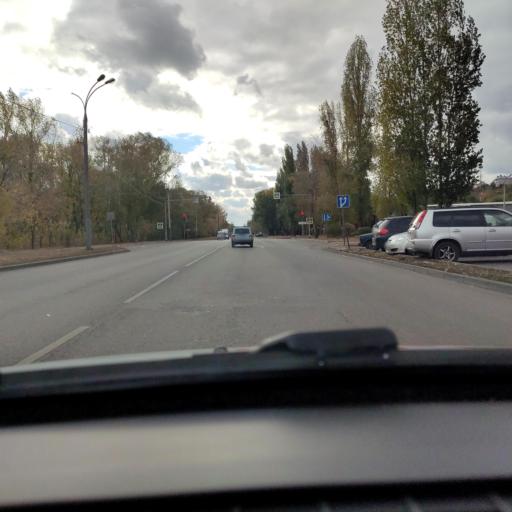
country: RU
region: Voronezj
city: Voronezh
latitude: 51.6520
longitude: 39.2118
